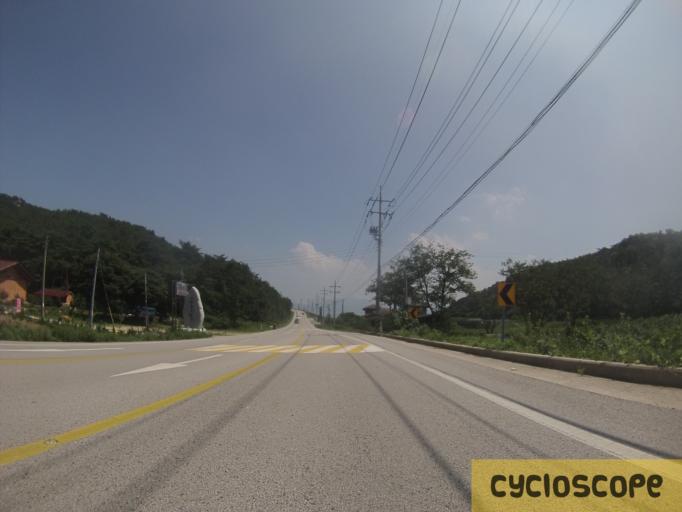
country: KR
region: Jeollabuk-do
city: Puan
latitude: 35.6556
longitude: 126.5440
